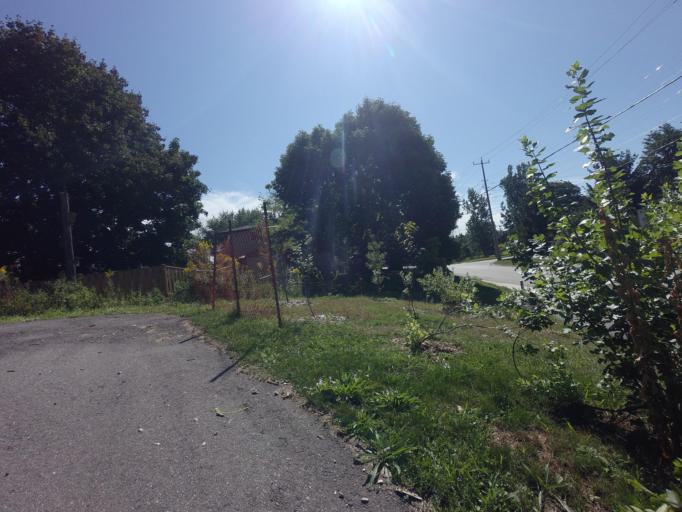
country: CA
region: Ontario
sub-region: Wellington County
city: Guelph
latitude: 43.7138
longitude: -80.3786
